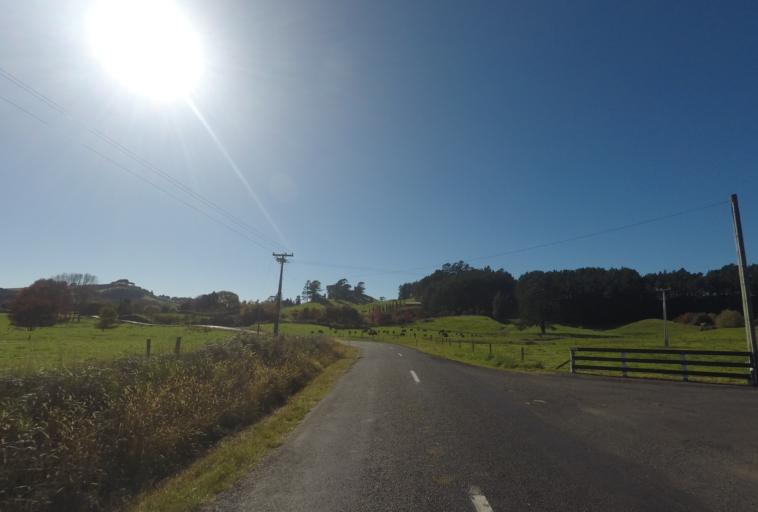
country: NZ
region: Bay of Plenty
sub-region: Western Bay of Plenty District
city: Waihi Beach
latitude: -37.4057
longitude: 175.9038
